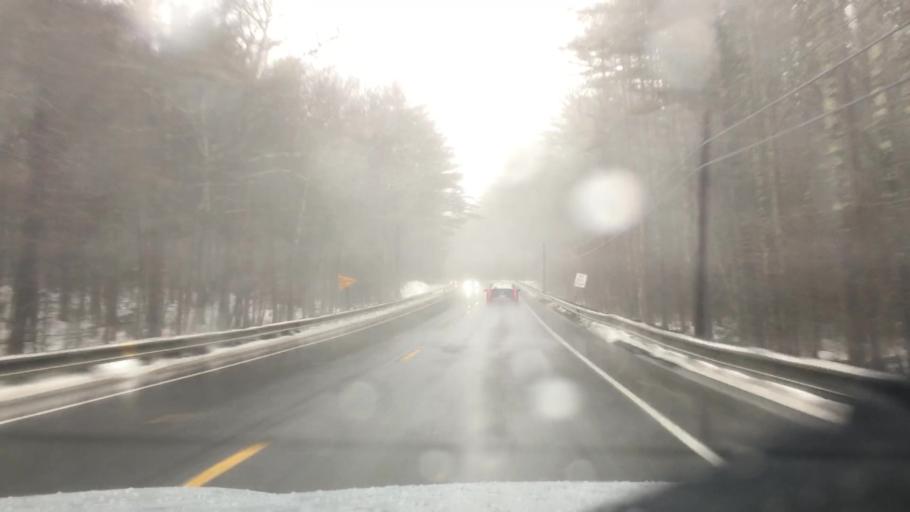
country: US
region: Massachusetts
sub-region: Franklin County
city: Orange
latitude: 42.5287
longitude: -72.3200
